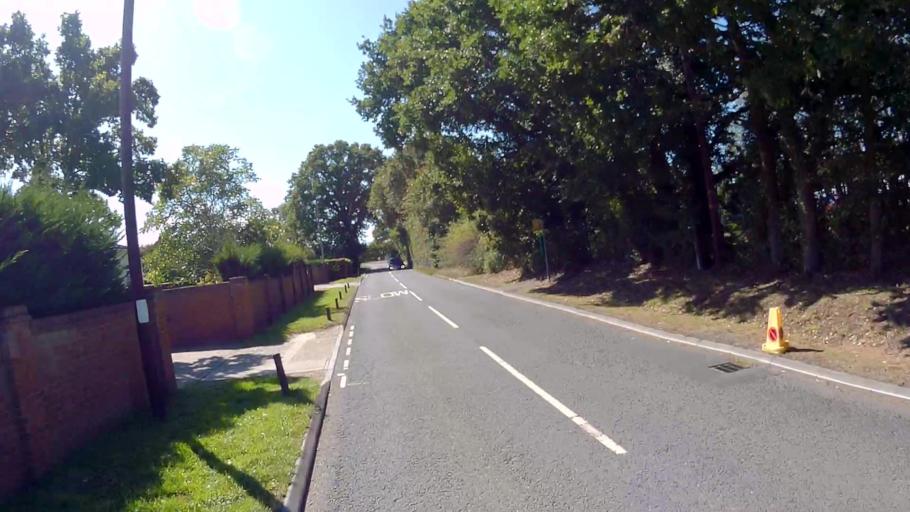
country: GB
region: England
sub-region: Hampshire
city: Eversley
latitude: 51.3773
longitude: -0.8880
